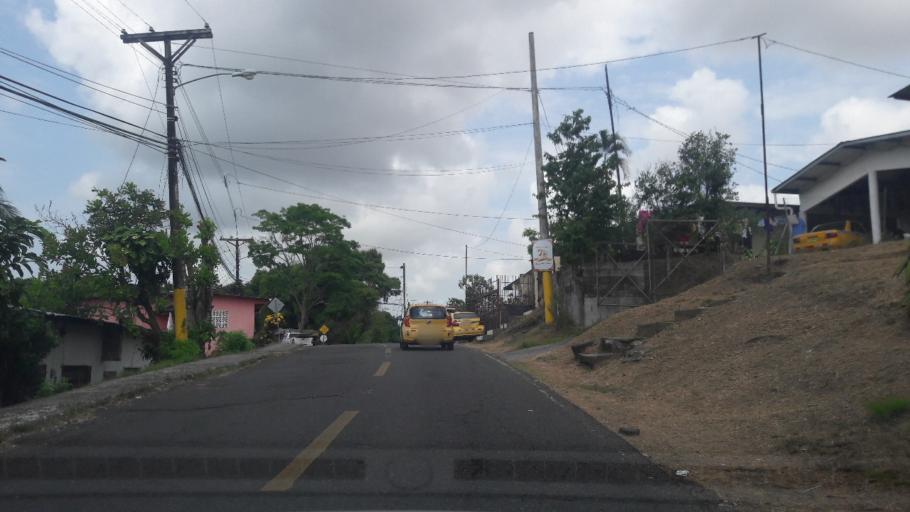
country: PA
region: Panama
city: Alcalde Diaz
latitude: 9.1170
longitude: -79.5547
